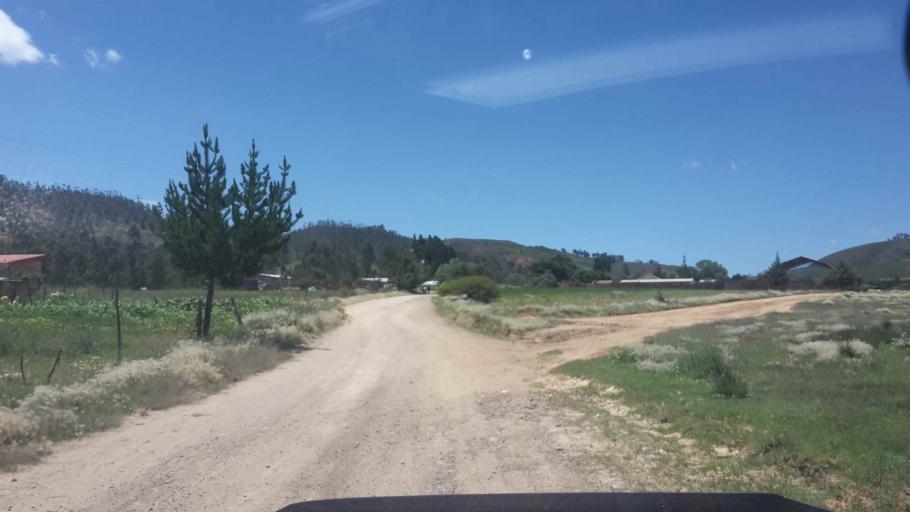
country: BO
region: Cochabamba
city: Totora
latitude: -17.7635
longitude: -65.2263
